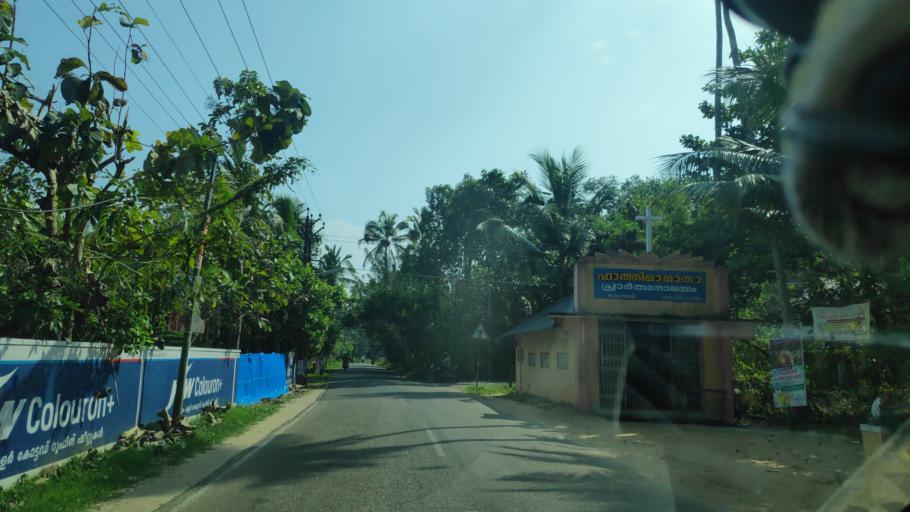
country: IN
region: Kerala
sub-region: Alappuzha
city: Shertallai
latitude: 9.6274
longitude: 76.2998
